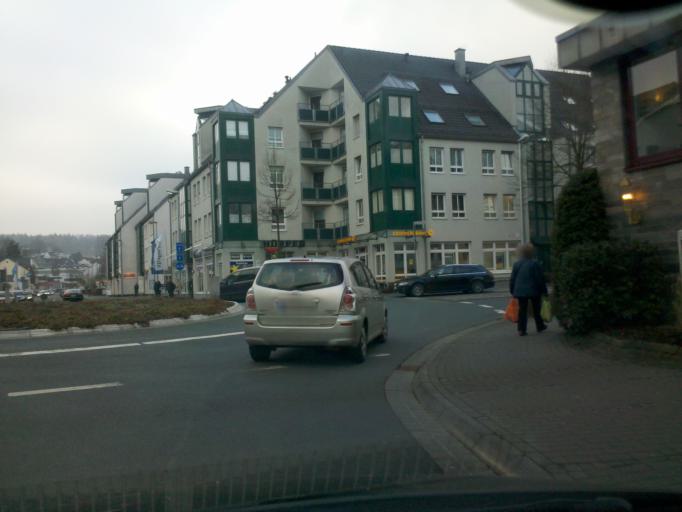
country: DE
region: North Rhine-Westphalia
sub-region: Regierungsbezirk Arnsberg
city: Olpe
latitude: 51.0263
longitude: 7.8438
